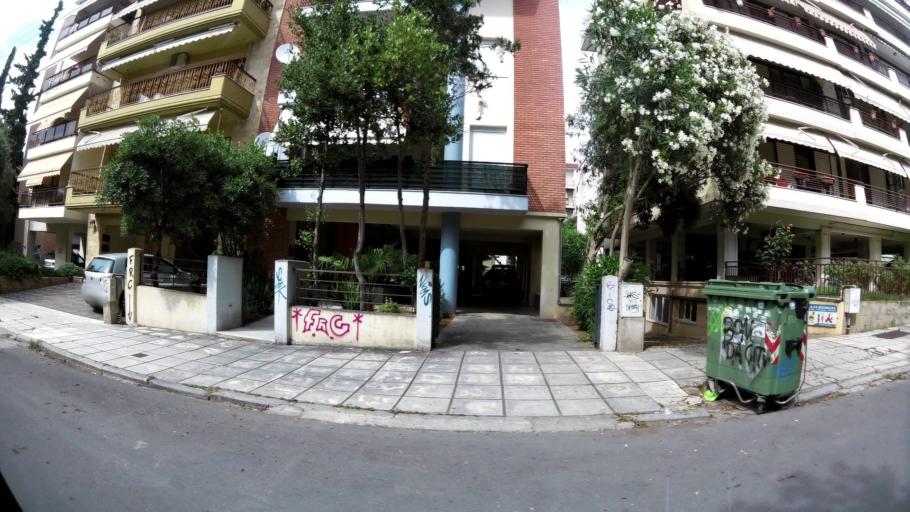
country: GR
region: Central Macedonia
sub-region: Nomos Thessalonikis
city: Kalamaria
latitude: 40.5865
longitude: 22.9445
